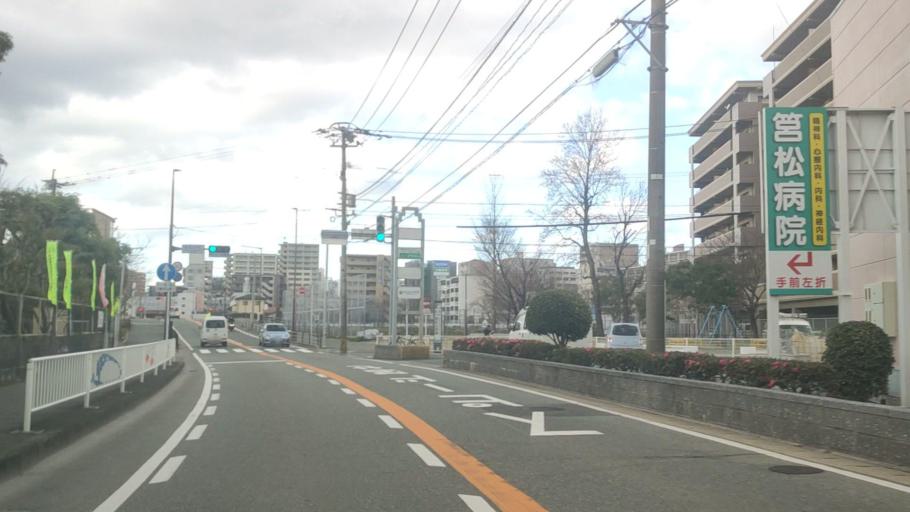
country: JP
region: Fukuoka
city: Fukuoka-shi
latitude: 33.6166
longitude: 130.4313
